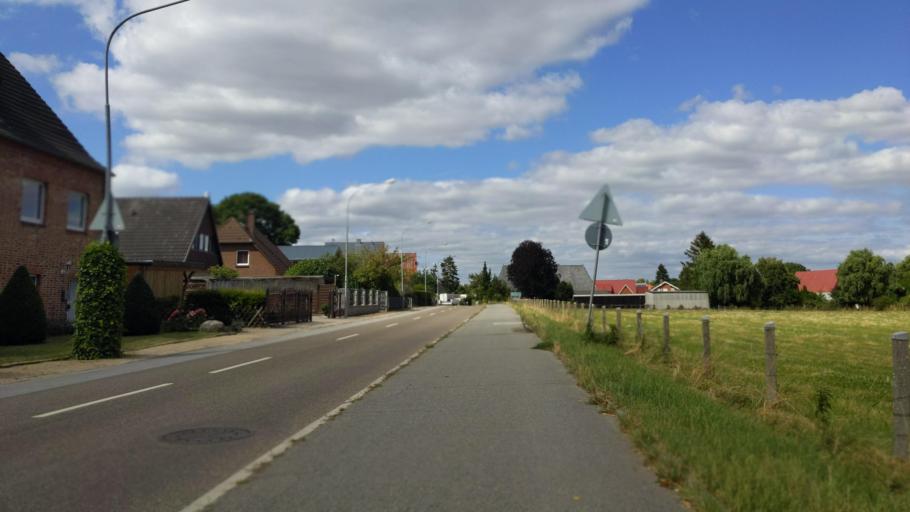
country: DE
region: Schleswig-Holstein
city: Stockelsdorf
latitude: 53.8745
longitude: 10.6153
